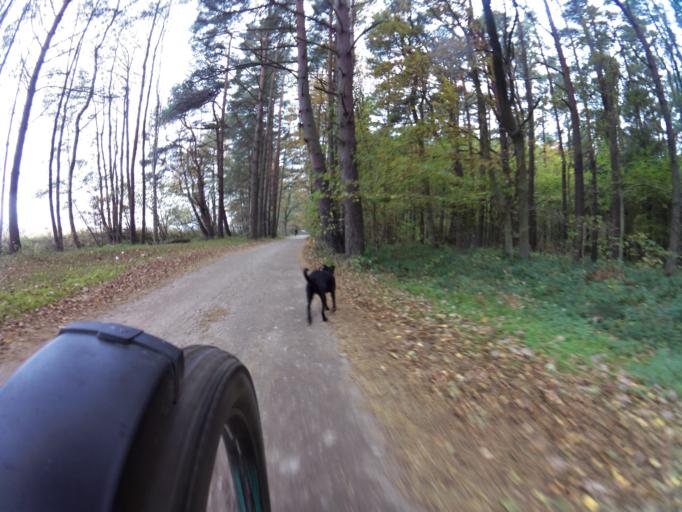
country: PL
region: Pomeranian Voivodeship
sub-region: Powiat pucki
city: Krokowa
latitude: 54.8290
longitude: 18.1290
